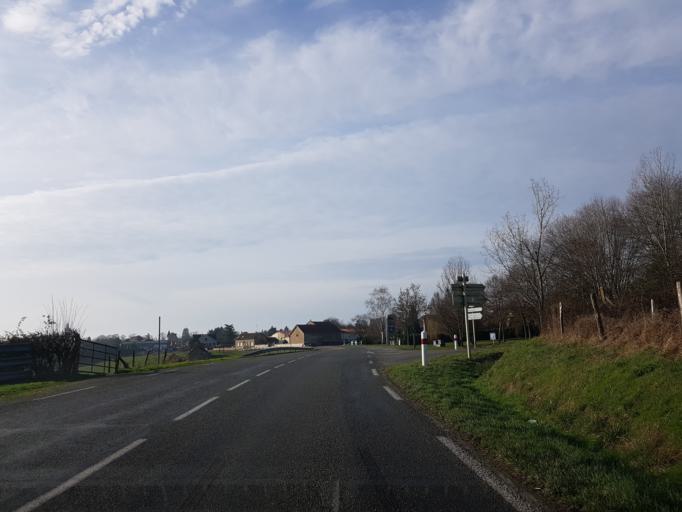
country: FR
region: Bourgogne
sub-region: Departement de Saone-et-Loire
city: Bourbon-Lancy
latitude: 46.6253
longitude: 3.7850
